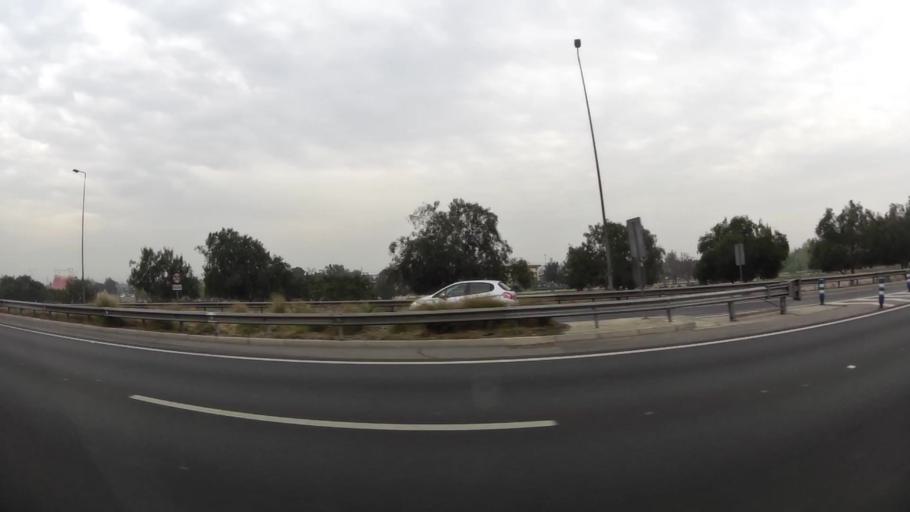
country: CL
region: Santiago Metropolitan
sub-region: Provincia de Santiago
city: Lo Prado
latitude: -33.4117
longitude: -70.7244
